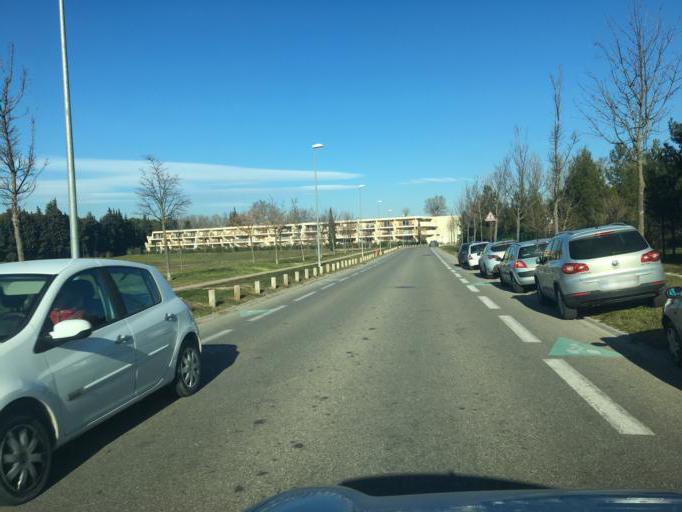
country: FR
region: Provence-Alpes-Cote d'Azur
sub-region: Departement du Vaucluse
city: Montfavet
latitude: 43.9180
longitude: 4.8888
